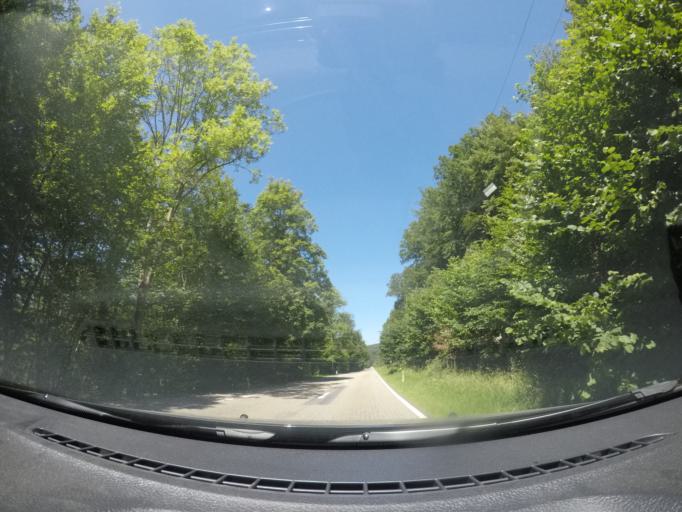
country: BE
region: Wallonia
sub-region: Province du Luxembourg
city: Daverdisse
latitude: 50.0485
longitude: 5.1372
